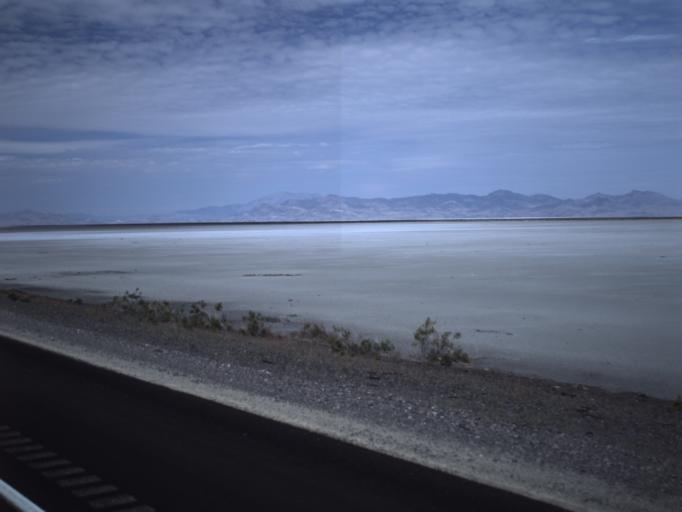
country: US
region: Utah
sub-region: Tooele County
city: Wendover
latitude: 40.7327
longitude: -113.5368
